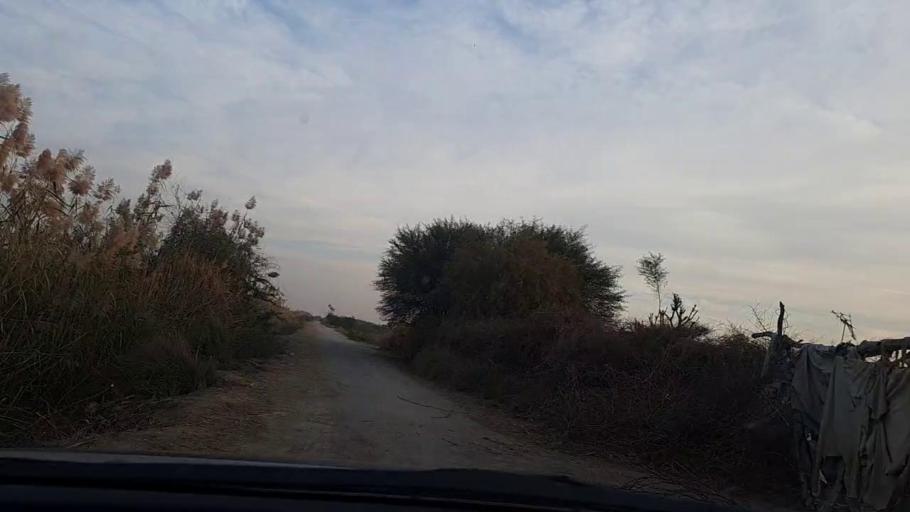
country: PK
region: Sindh
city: Sakrand
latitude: 26.1792
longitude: 68.3422
